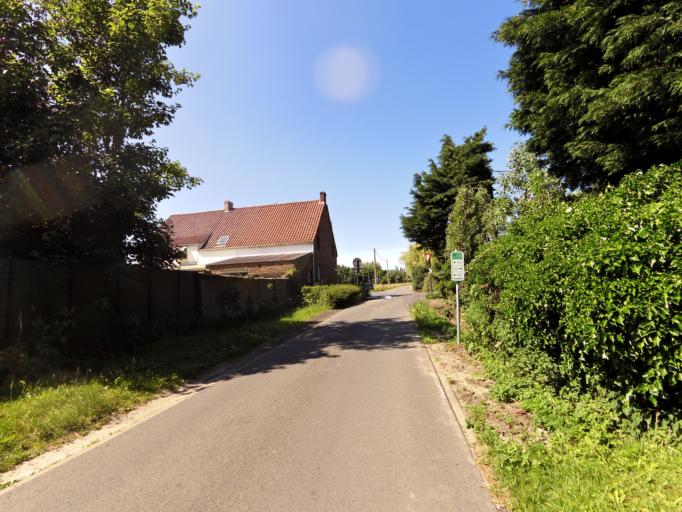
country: BE
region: Flanders
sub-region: Provincie West-Vlaanderen
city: Oudenburg
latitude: 51.1598
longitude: 3.0333
